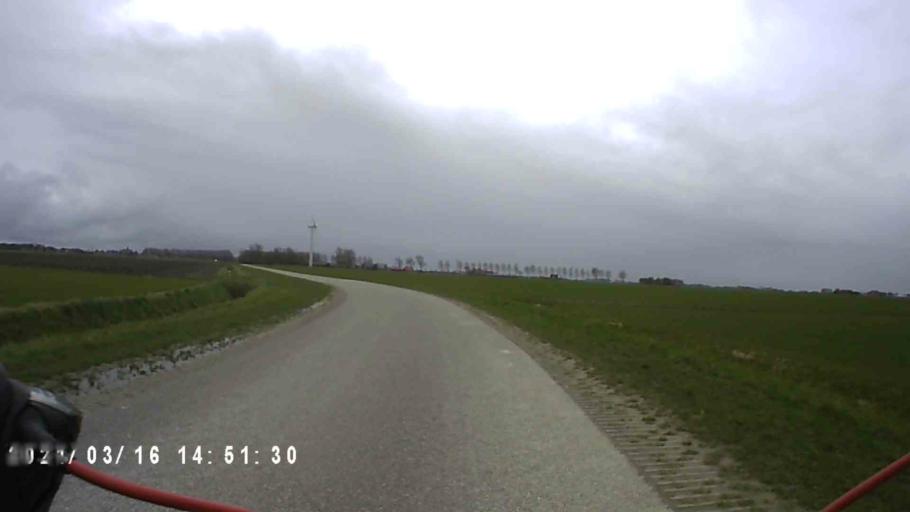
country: NL
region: Friesland
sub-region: Gemeente Harlingen
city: Harlingen
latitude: 53.1161
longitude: 5.4647
